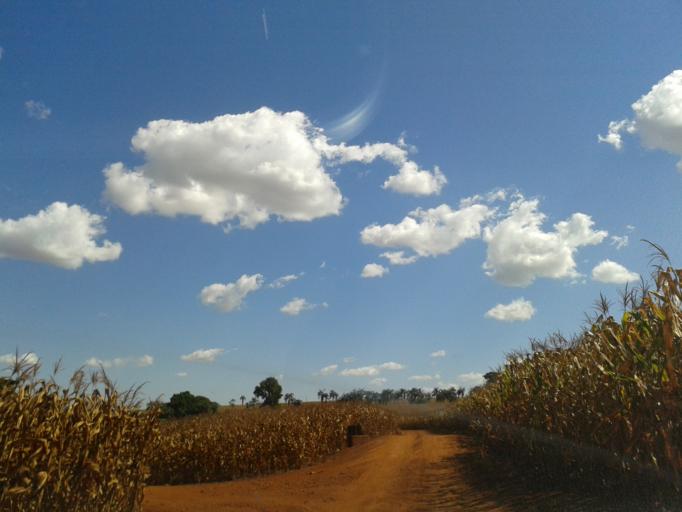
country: BR
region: Minas Gerais
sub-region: Capinopolis
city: Capinopolis
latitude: -18.6275
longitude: -49.4739
